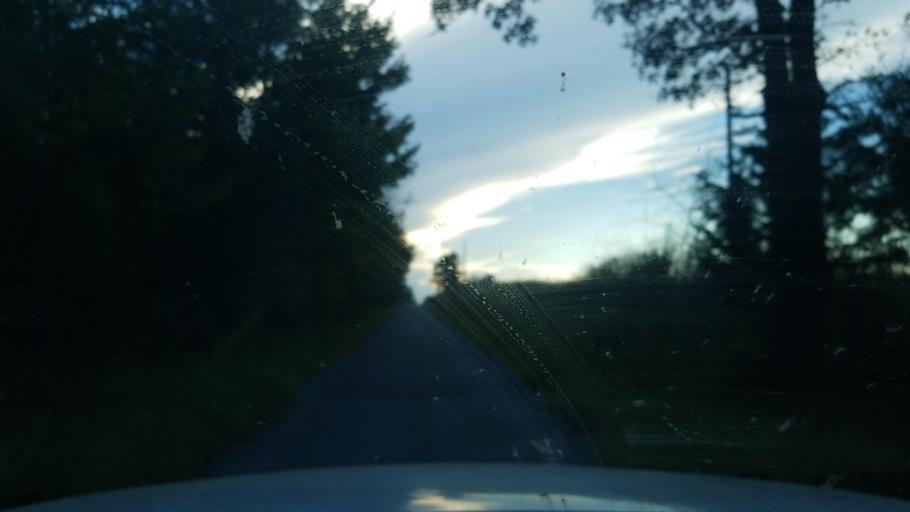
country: US
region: Illinois
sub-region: Saline County
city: Carrier Mills
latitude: 37.7903
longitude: -88.6980
